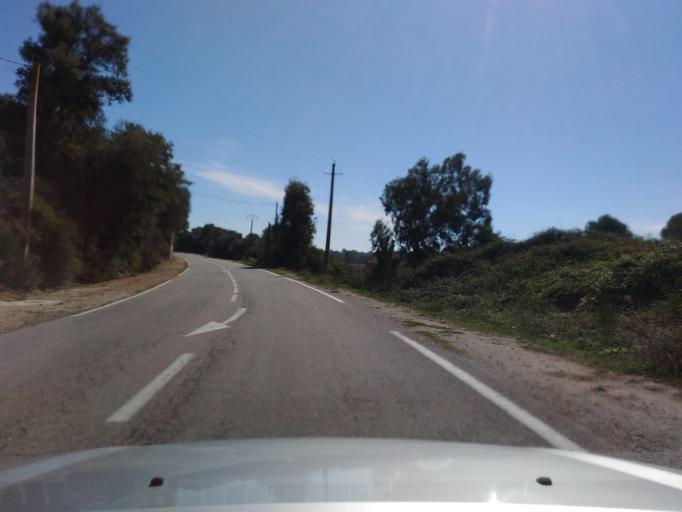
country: FR
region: Corsica
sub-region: Departement de la Haute-Corse
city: Aleria
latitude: 42.1157
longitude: 9.4918
